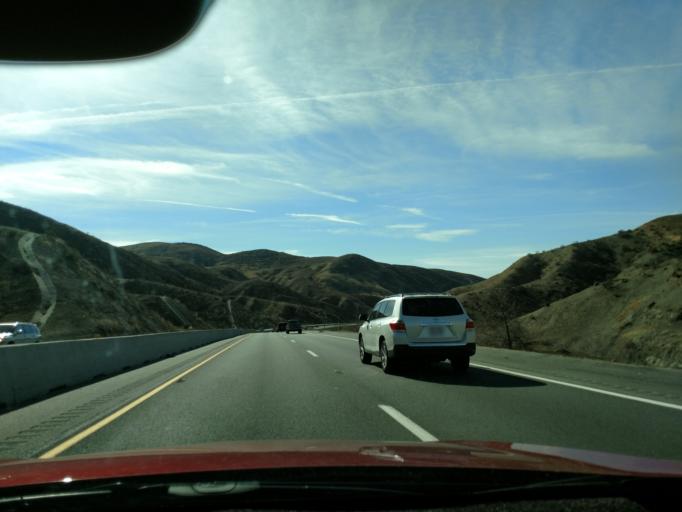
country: US
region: California
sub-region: Riverside County
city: Beaumont
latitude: 33.8740
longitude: -116.9929
